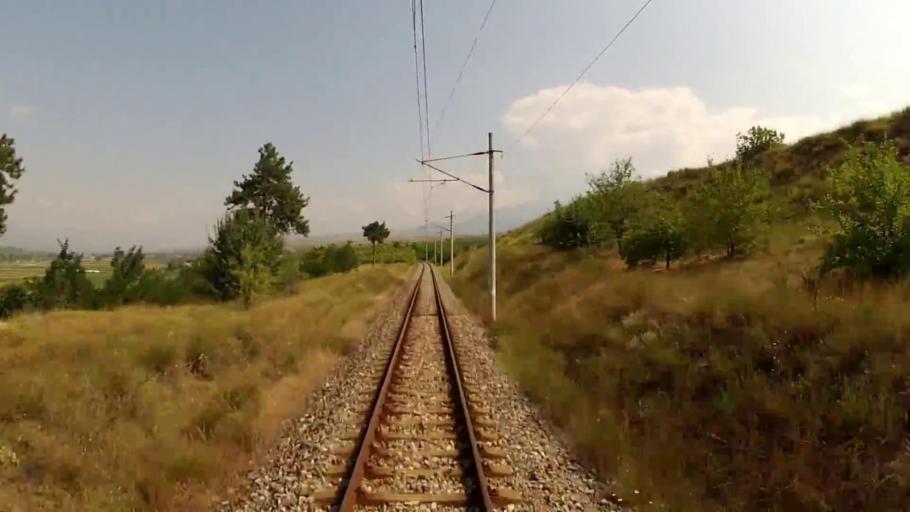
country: BG
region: Blagoevgrad
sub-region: Obshtina Sandanski
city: Sandanski
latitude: 41.5732
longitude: 23.2415
